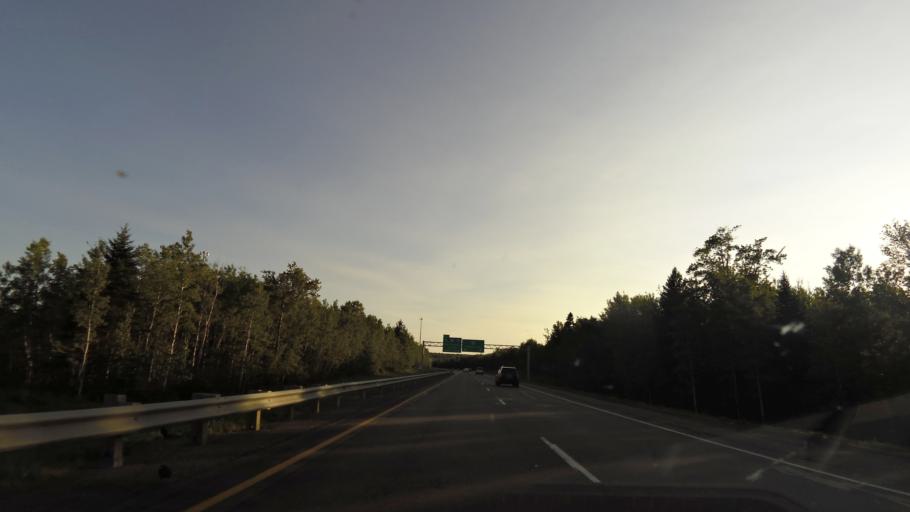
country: CA
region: New Brunswick
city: Salisbury
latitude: 46.0011
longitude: -65.1335
